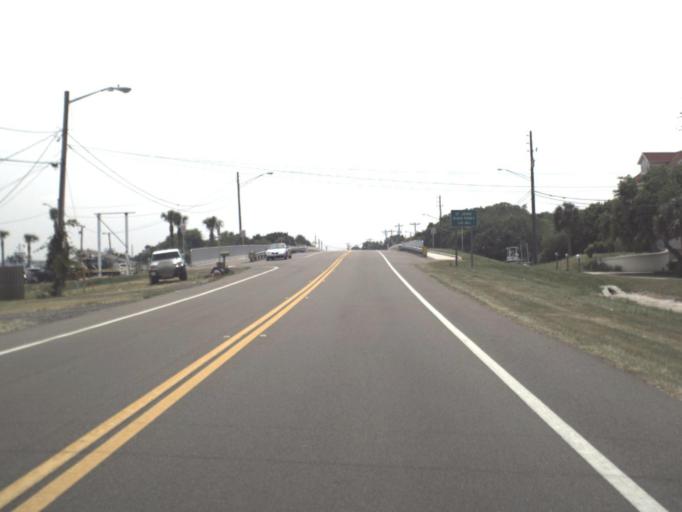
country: US
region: Florida
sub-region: Duval County
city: Atlantic Beach
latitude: 30.3985
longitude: -81.4351
